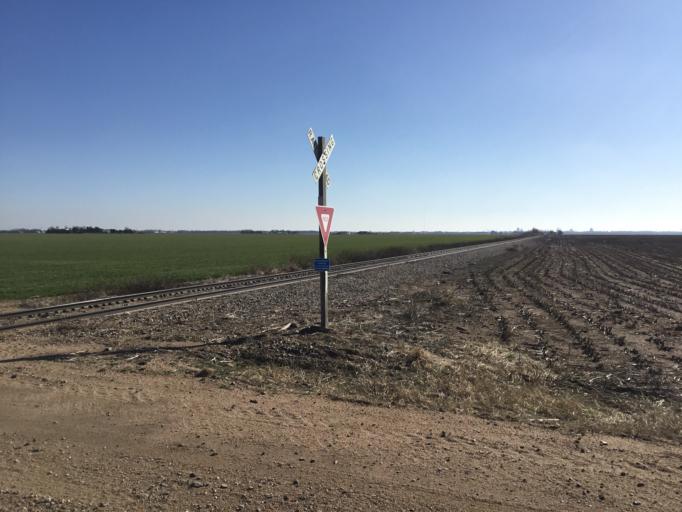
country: US
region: Kansas
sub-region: Sedgwick County
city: Colwich
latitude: 37.7858
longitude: -97.6080
